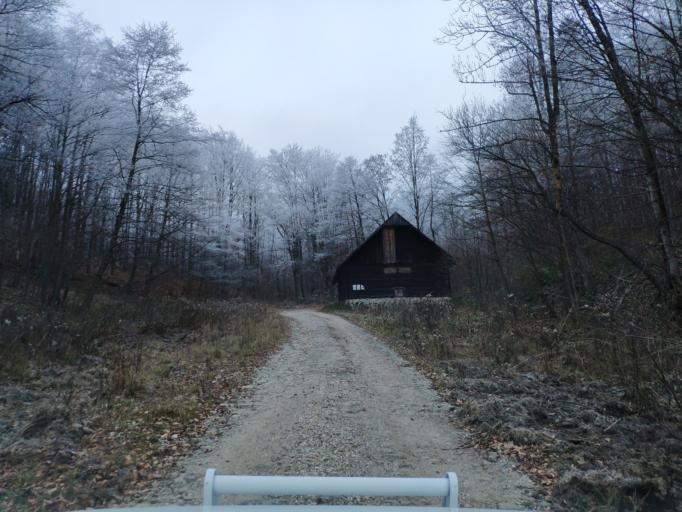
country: SK
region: Kosicky
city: Dobsina
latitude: 48.7988
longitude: 20.4757
